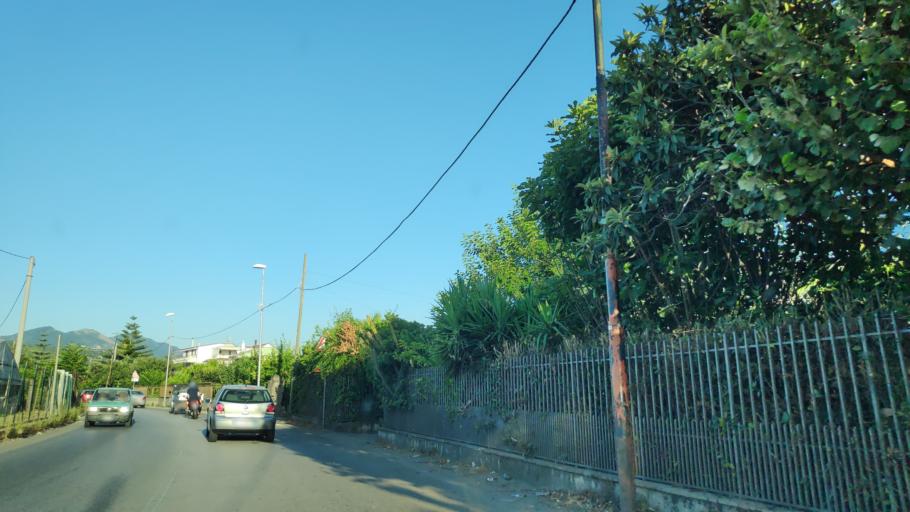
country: IT
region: Campania
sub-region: Provincia di Salerno
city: Pagani
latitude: 40.7630
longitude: 14.6131
